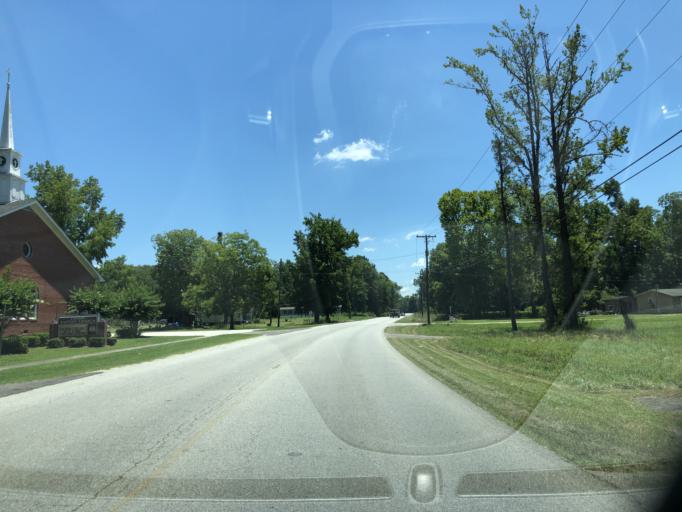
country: US
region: South Carolina
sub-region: Orangeburg County
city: Branchville
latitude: 33.2513
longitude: -80.8093
